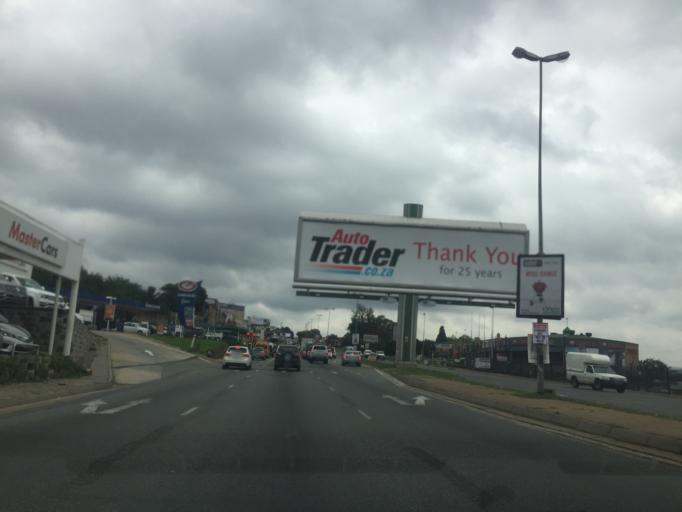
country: ZA
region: Gauteng
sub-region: City of Johannesburg Metropolitan Municipality
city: Roodepoort
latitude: -26.0752
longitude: 27.9750
